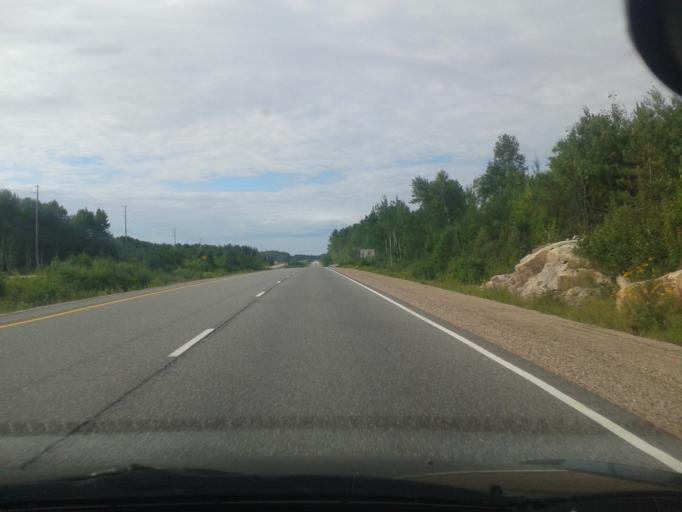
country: CA
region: Ontario
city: Powassan
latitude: 46.1569
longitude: -79.3594
